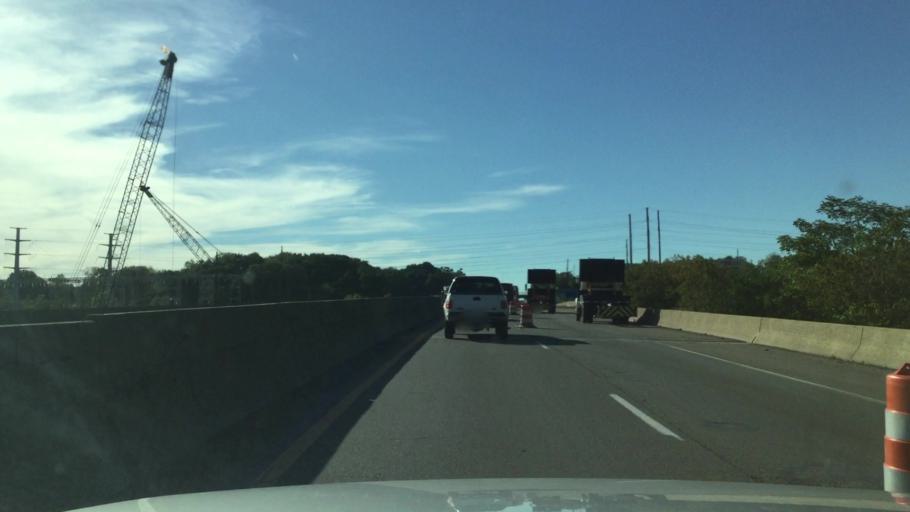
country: US
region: Michigan
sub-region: Jackson County
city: Jackson
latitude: 42.2716
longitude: -84.4069
